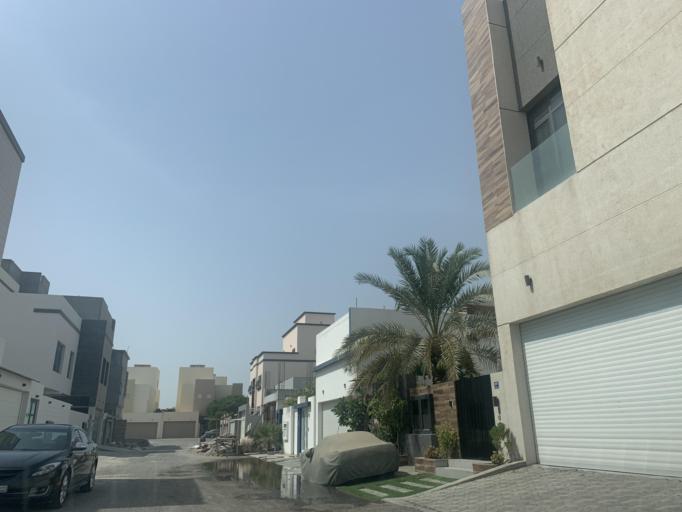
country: BH
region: Northern
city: Madinat `Isa
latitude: 26.1861
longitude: 50.4910
